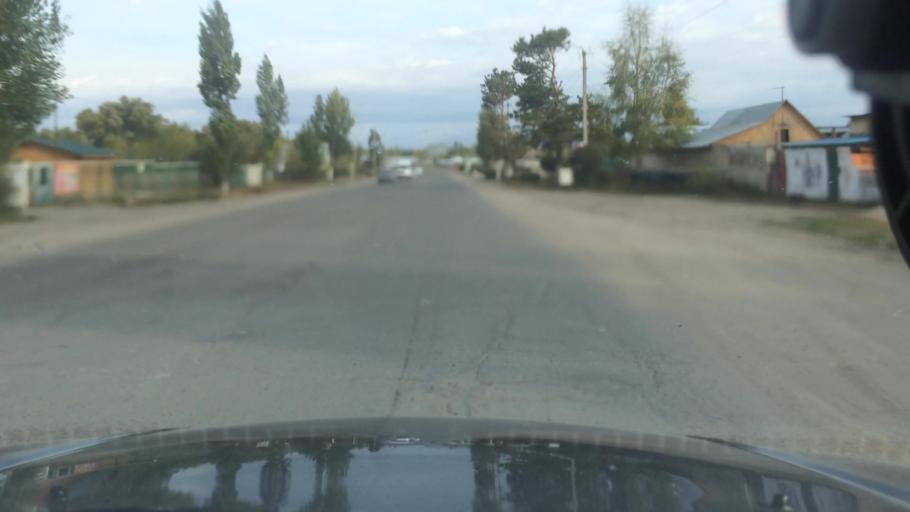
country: KG
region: Ysyk-Koel
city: Karakol
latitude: 42.5207
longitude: 78.3859
